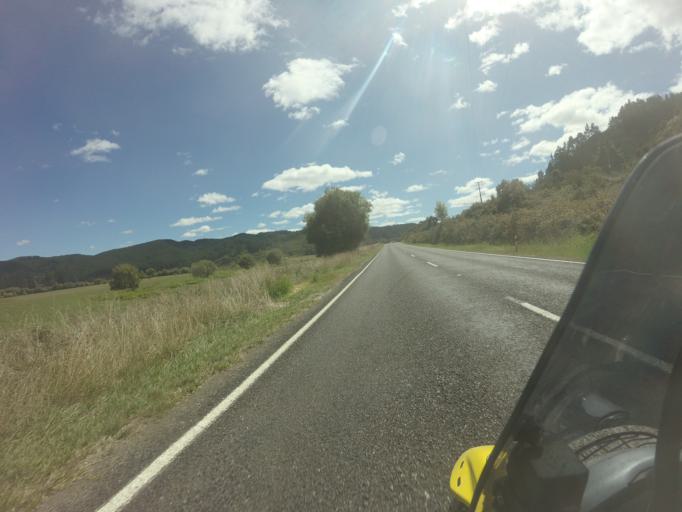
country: NZ
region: Bay of Plenty
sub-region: Kawerau District
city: Kawerau
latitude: -38.1895
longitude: 176.8398
